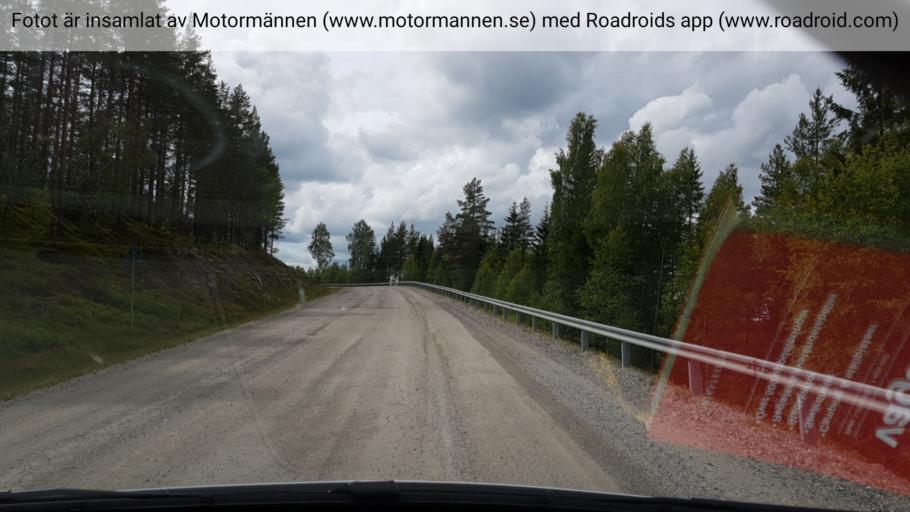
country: SE
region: Vaesternorrland
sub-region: Solleftea Kommun
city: Solleftea
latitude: 63.3834
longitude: 17.4973
